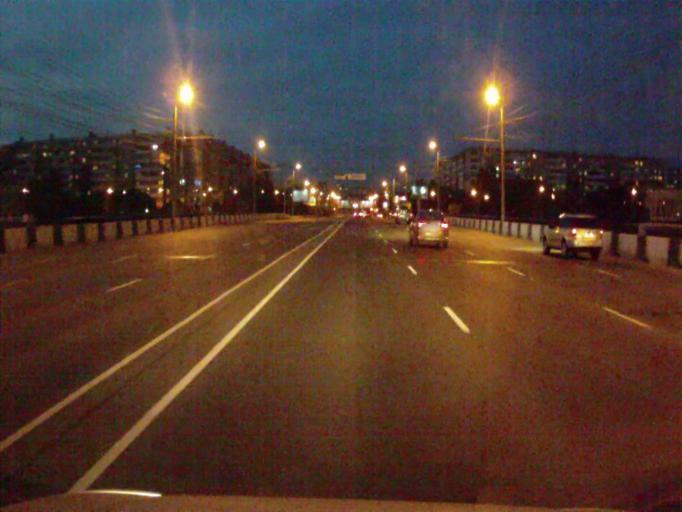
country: RU
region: Chelyabinsk
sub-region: Gorod Chelyabinsk
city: Chelyabinsk
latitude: 55.1738
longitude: 61.3582
